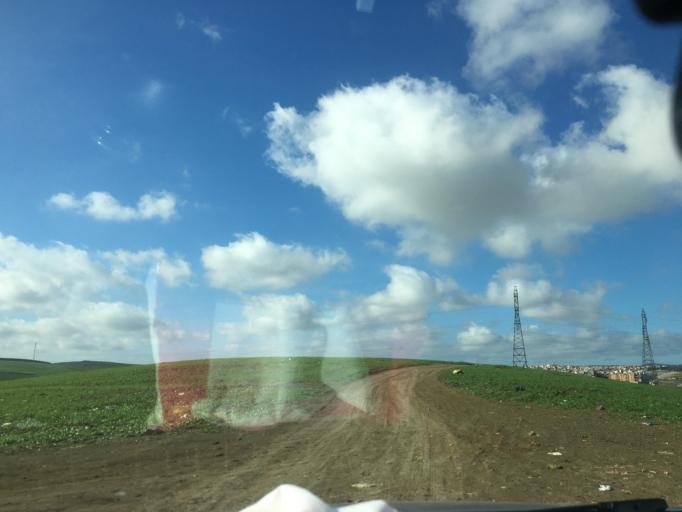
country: MA
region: Tanger-Tetouan
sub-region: Tanger-Assilah
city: Tangier
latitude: 35.7155
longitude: -5.8145
